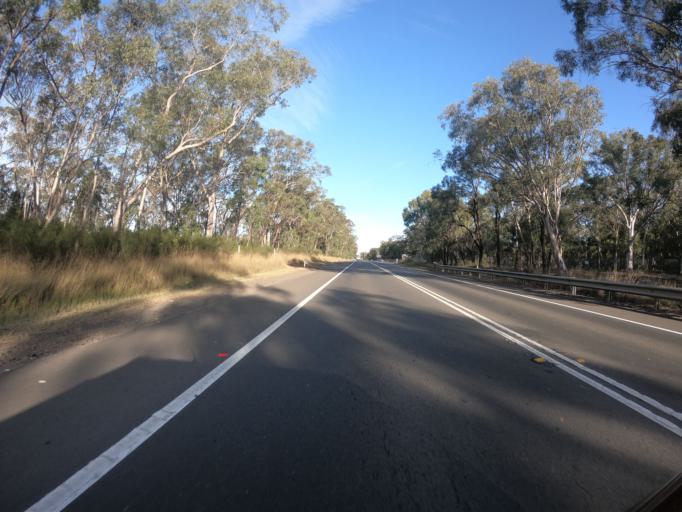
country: AU
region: New South Wales
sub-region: Hawkesbury
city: South Windsor
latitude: -33.6519
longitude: 150.7928
